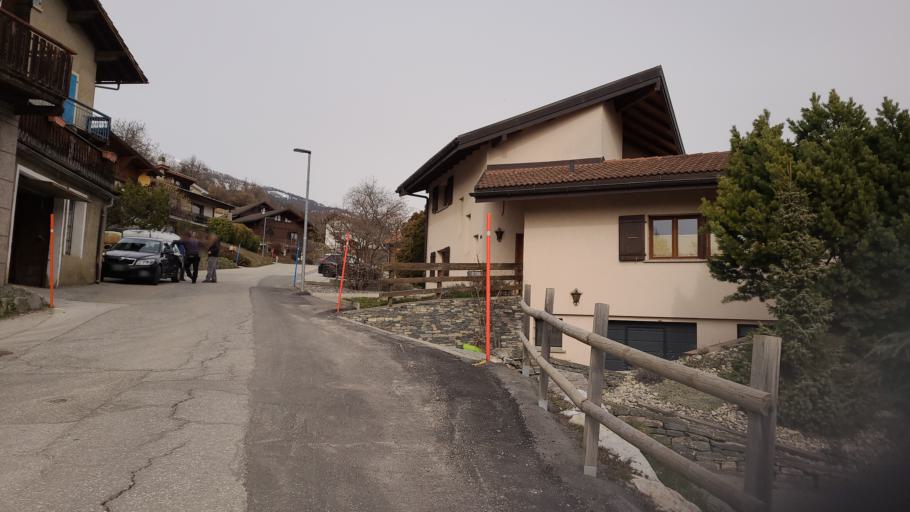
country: CH
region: Valais
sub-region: Herens District
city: Ayent
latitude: 46.2755
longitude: 7.4108
